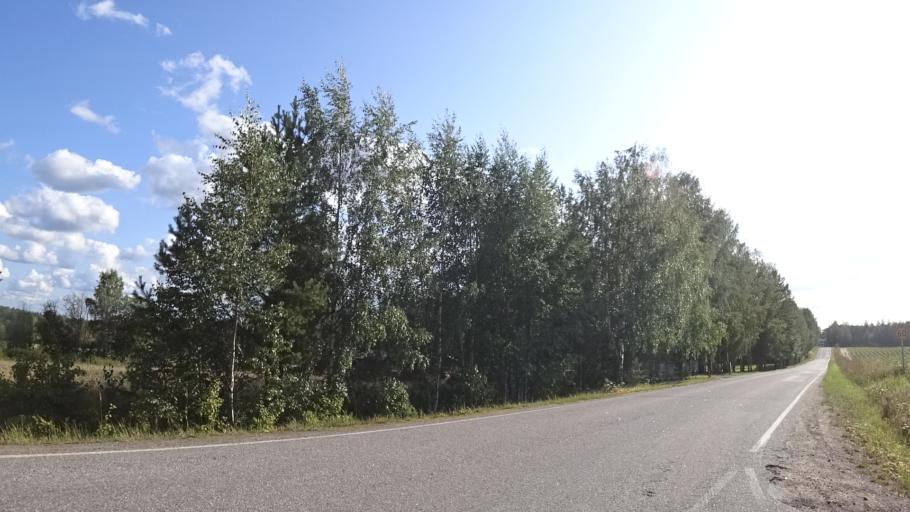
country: FI
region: North Karelia
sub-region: Keski-Karjala
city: Kesaelahti
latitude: 61.8946
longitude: 29.8501
